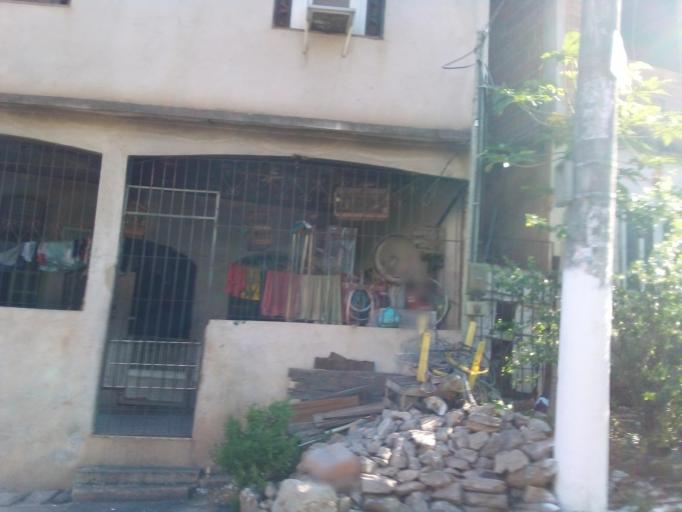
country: BR
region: Espirito Santo
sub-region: Vitoria
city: Vitoria
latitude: -20.3085
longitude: -40.3739
